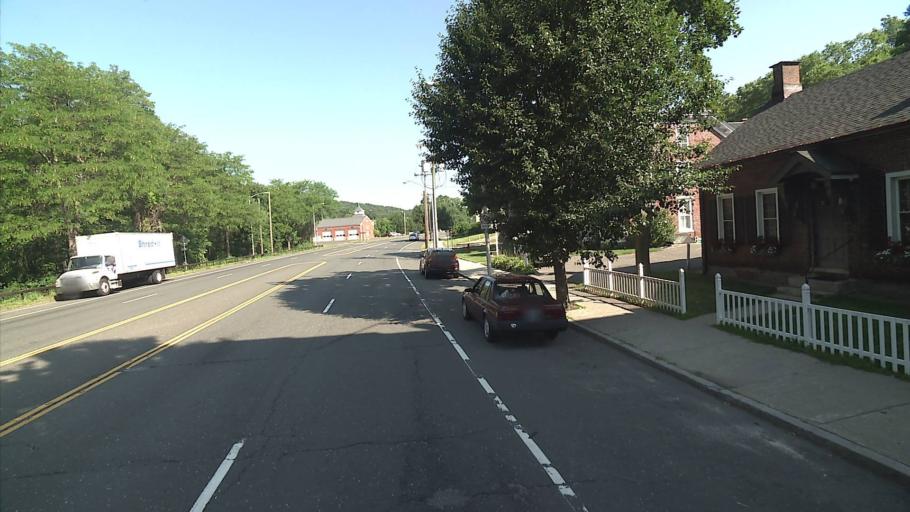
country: US
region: Connecticut
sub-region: Litchfield County
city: Winsted
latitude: 41.9224
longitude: -73.0750
